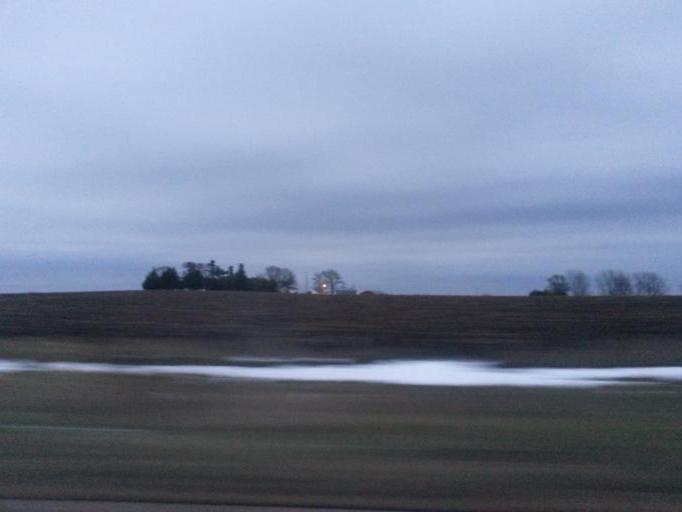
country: US
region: Iowa
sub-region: Black Hawk County
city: Elk Run Heights
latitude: 42.4232
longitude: -92.1845
